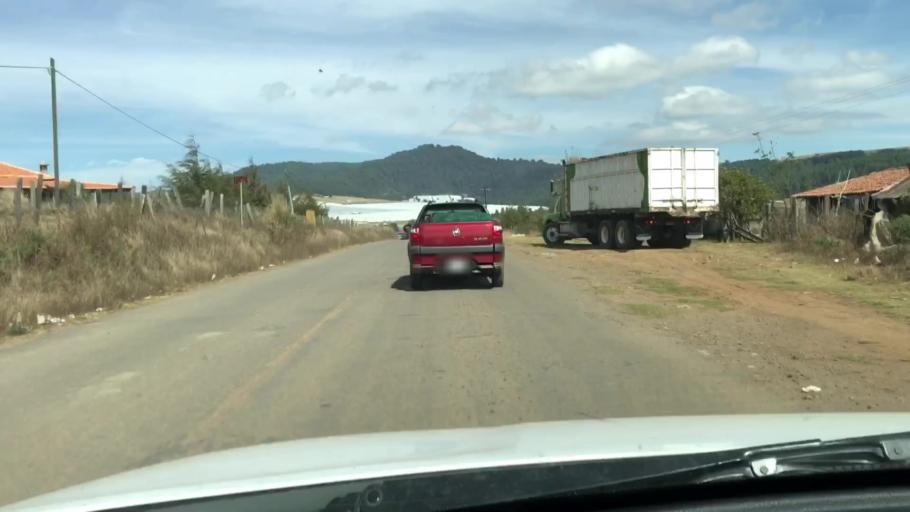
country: MX
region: Jalisco
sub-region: Amacueca
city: Tepec
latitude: 20.0199
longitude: -103.6895
